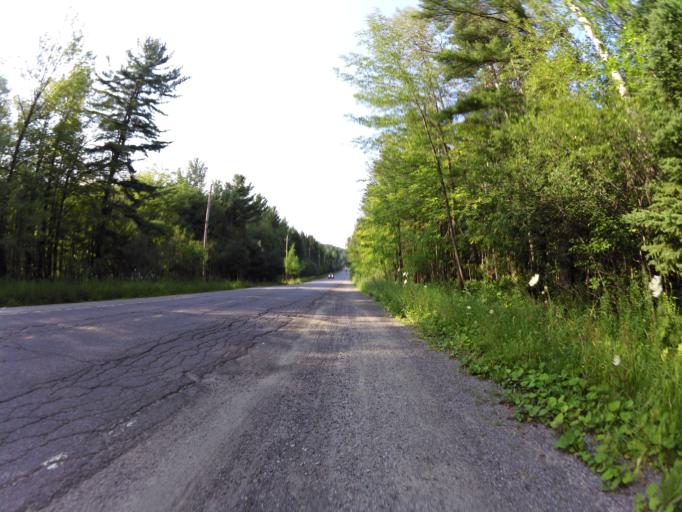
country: CA
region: Quebec
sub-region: Outaouais
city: Gatineau
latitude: 45.4908
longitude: -75.8133
